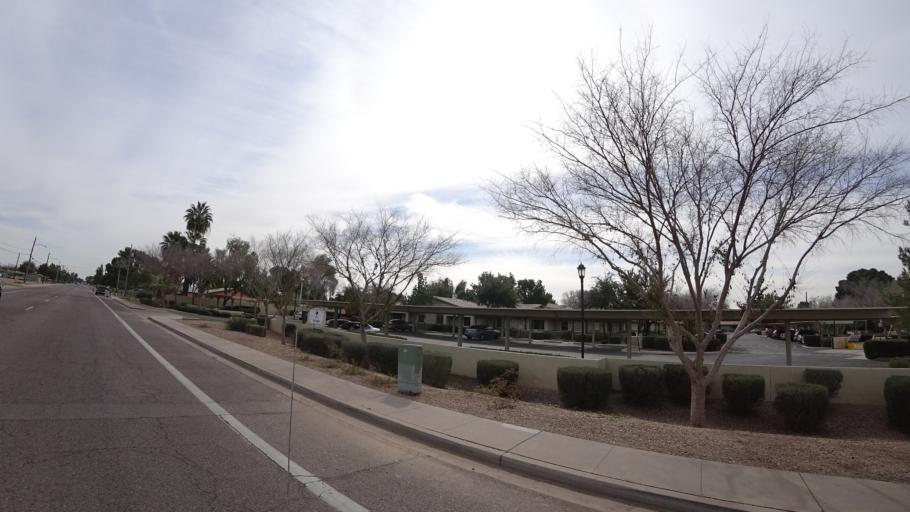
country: US
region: Arizona
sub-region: Maricopa County
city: Glendale
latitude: 33.5311
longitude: -112.2001
